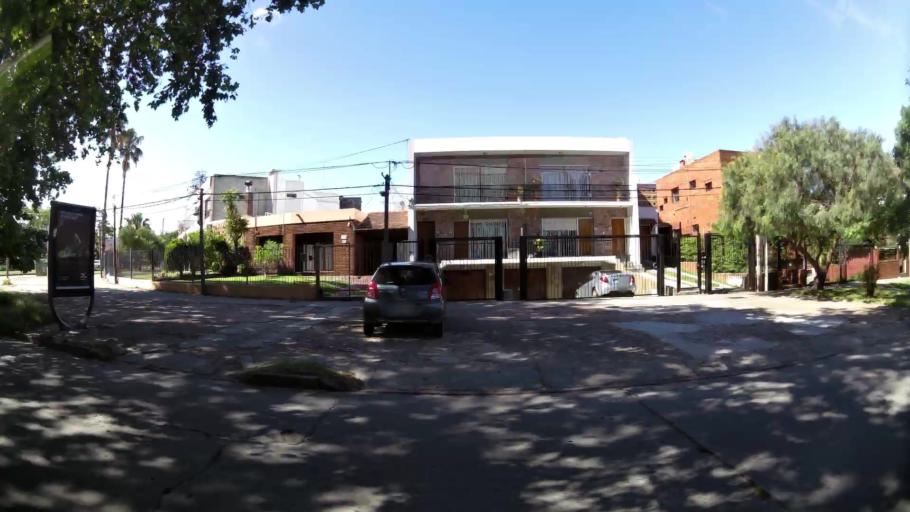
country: UY
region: Canelones
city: Paso de Carrasco
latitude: -34.8895
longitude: -56.1002
